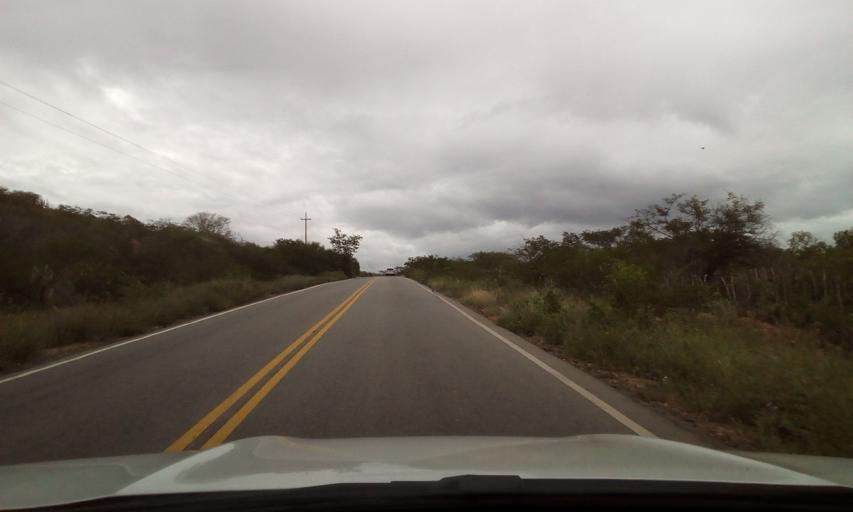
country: BR
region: Paraiba
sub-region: Picui
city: Picui
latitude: -6.5331
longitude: -36.3076
